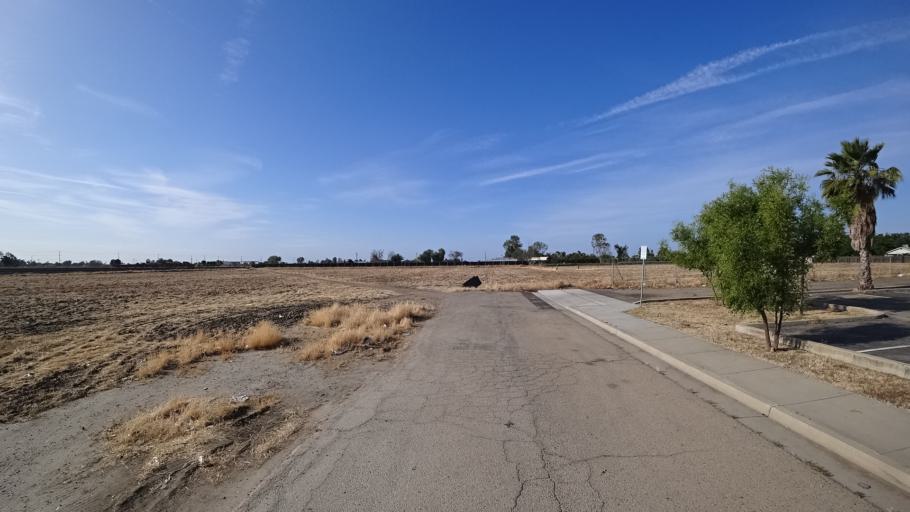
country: US
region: California
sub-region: Kings County
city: Hanford
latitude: 36.3120
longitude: -119.6506
